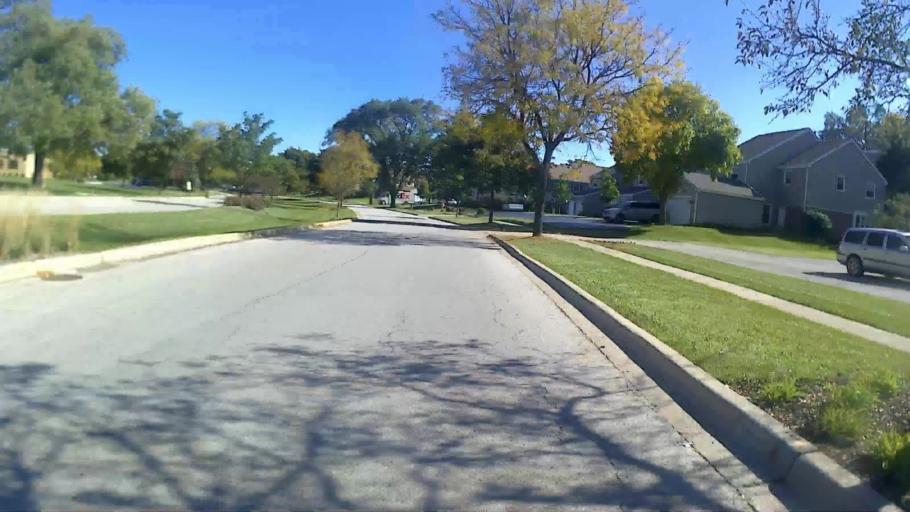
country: US
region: Illinois
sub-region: Cook County
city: Elk Grove Village
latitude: 42.0068
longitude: -87.9922
